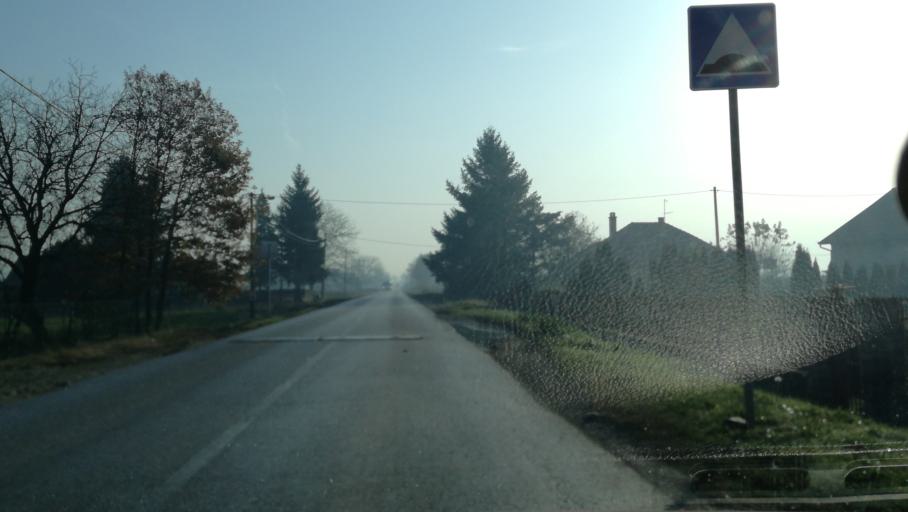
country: RS
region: Central Serbia
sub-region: Moravicki Okrug
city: Cacak
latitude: 43.9012
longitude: 20.4067
